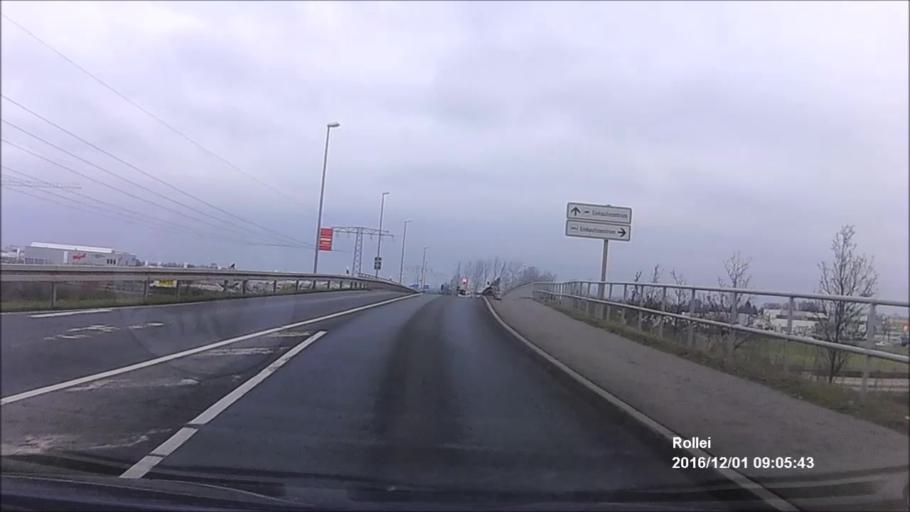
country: DE
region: Thuringia
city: Noda
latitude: 51.0317
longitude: 11.0017
